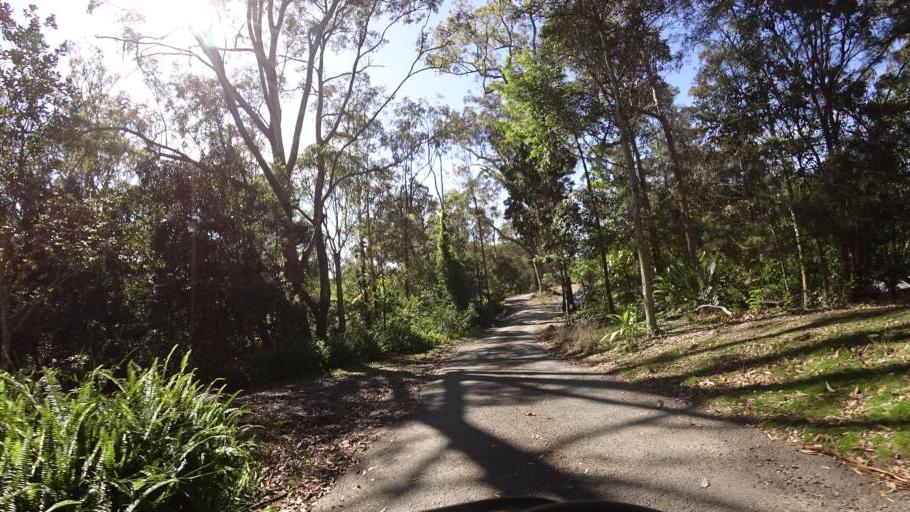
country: AU
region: Queensland
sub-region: Moreton Bay
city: Highvale
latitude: -27.4009
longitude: 152.7827
